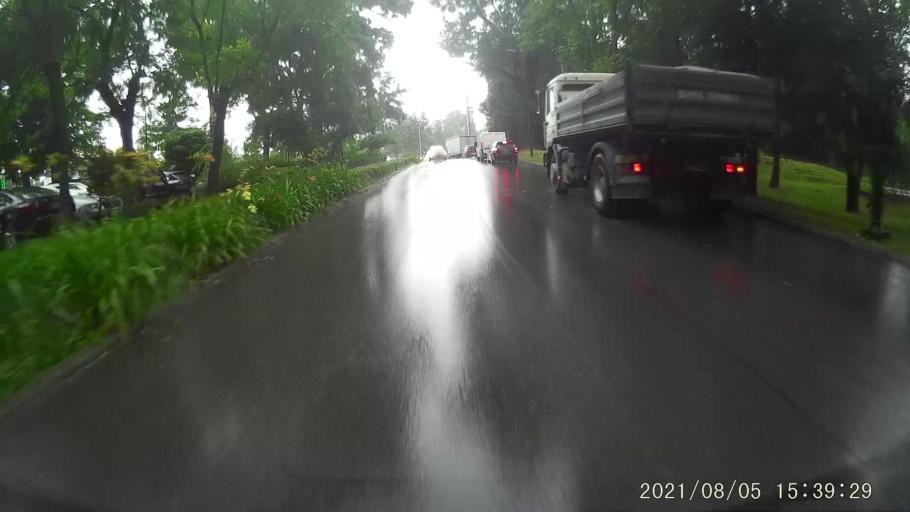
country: PL
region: Lower Silesian Voivodeship
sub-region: Powiat klodzki
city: Klodzko
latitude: 50.4396
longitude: 16.6496
